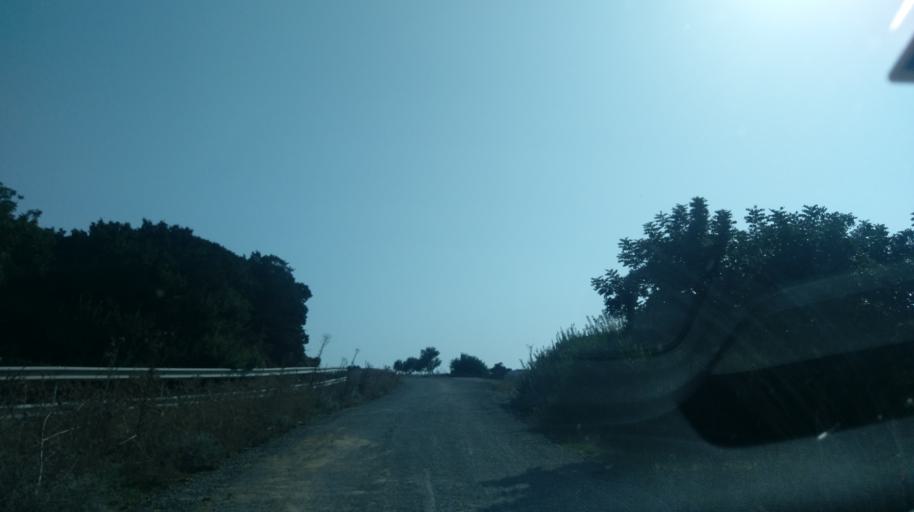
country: CY
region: Ammochostos
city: Rizokarpaso
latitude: 35.6461
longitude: 34.5537
